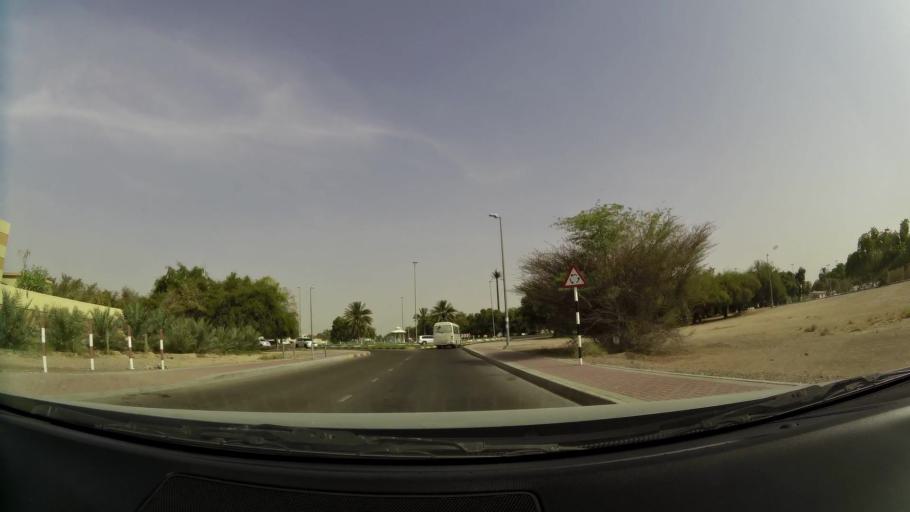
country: AE
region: Abu Dhabi
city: Al Ain
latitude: 24.1501
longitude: 55.6962
